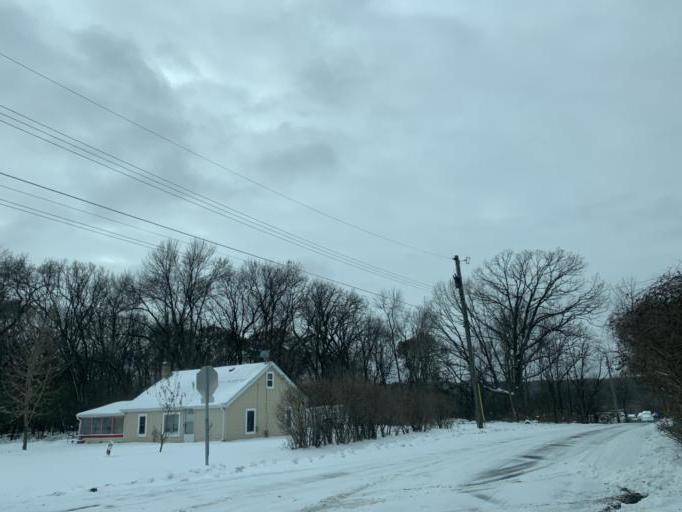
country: US
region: Minnesota
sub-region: Washington County
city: Saint Paul Park
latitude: 44.8423
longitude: -93.0024
